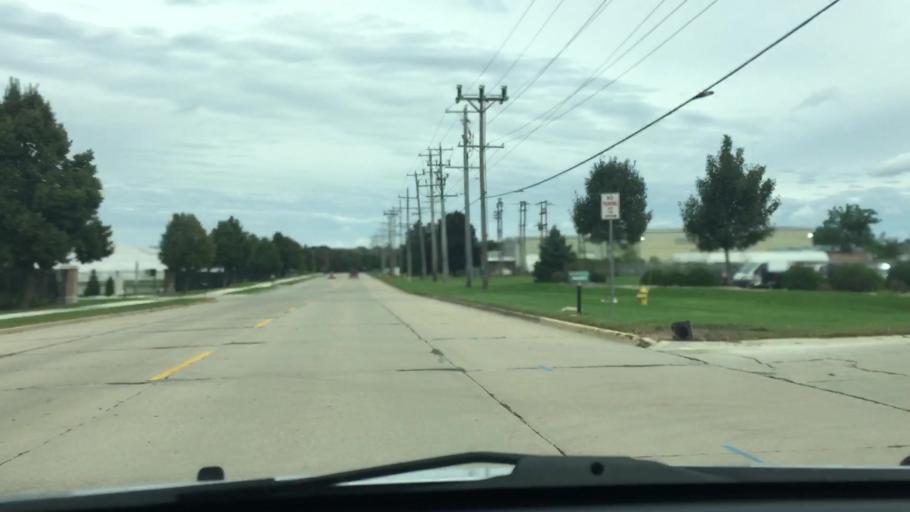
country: US
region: Wisconsin
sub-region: Waukesha County
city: Waukesha
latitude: 42.9976
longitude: -88.2490
